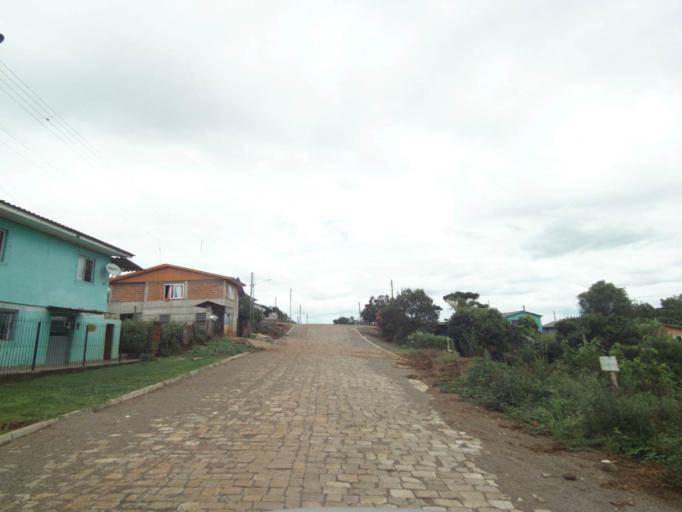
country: BR
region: Rio Grande do Sul
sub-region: Lagoa Vermelha
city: Lagoa Vermelha
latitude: -28.2171
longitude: -51.5399
